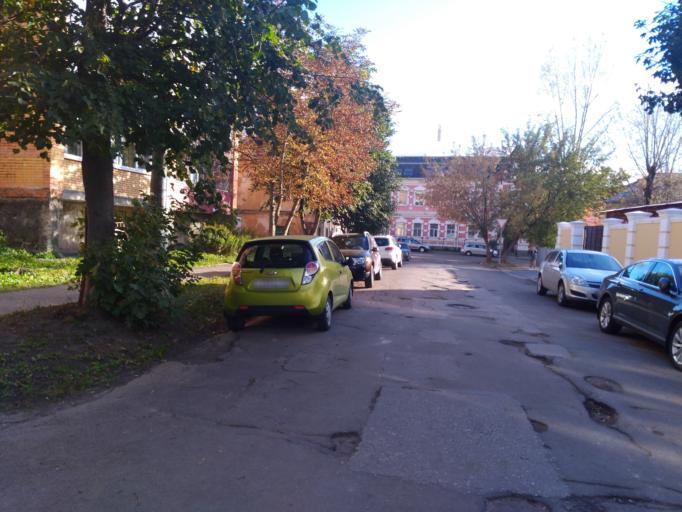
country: RU
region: Kaluga
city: Kaluga
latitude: 54.5104
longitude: 36.2526
